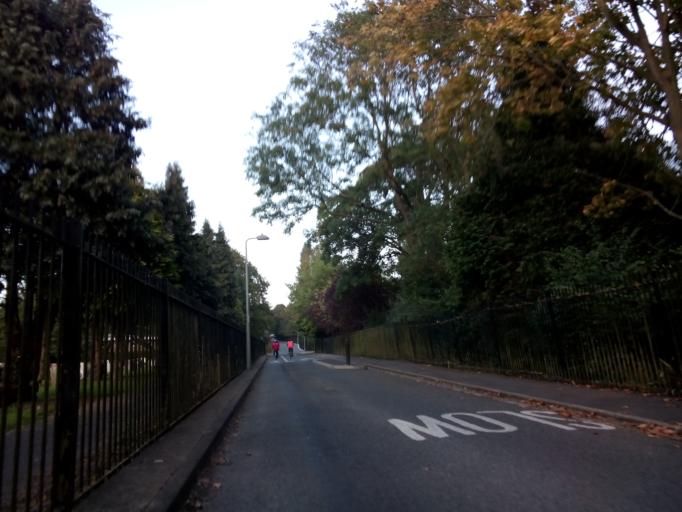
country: GB
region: England
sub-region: Suffolk
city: Ipswich
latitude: 52.0697
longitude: 1.1738
